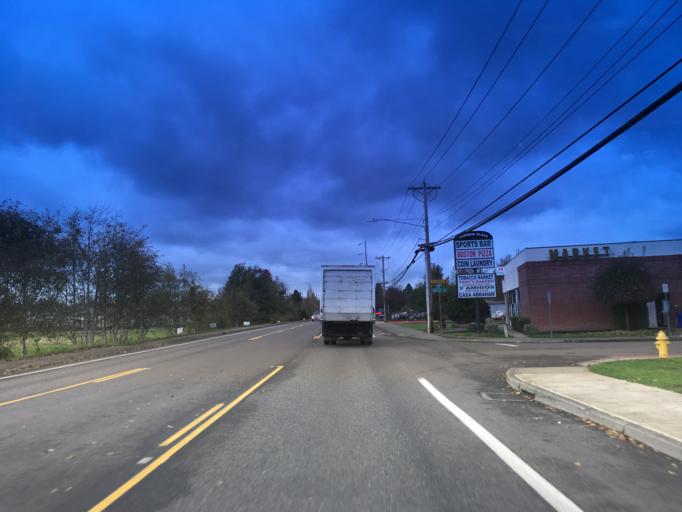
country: US
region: Oregon
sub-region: Multnomah County
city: Fairview
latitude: 45.5357
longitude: -122.4291
